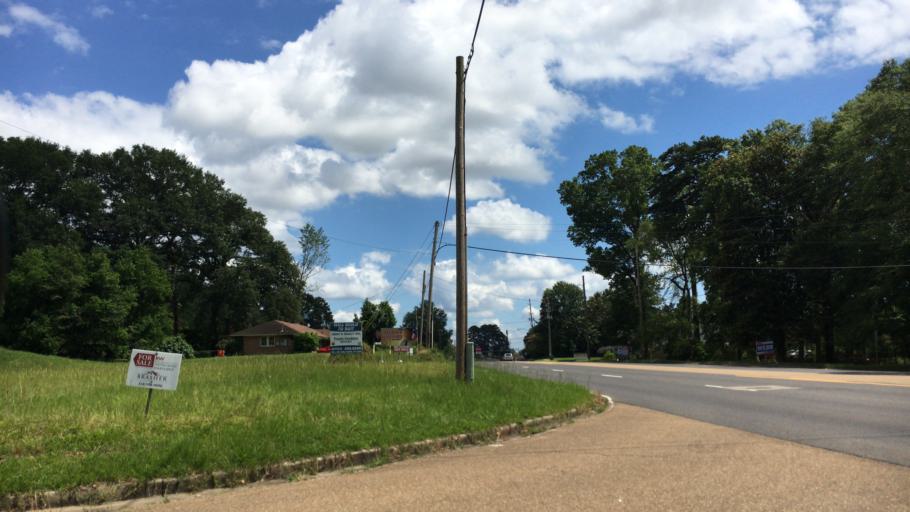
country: US
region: Louisiana
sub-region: Lincoln Parish
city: Ruston
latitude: 32.5480
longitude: -92.6399
